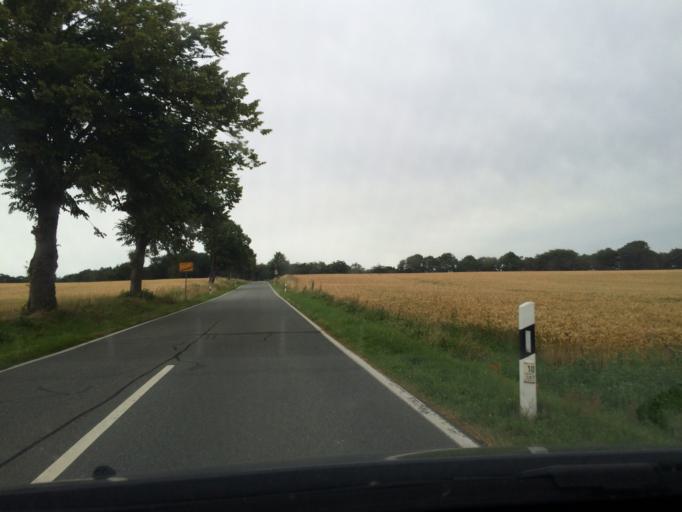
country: DE
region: Mecklenburg-Vorpommern
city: Prohn
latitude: 54.4164
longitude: 13.0147
